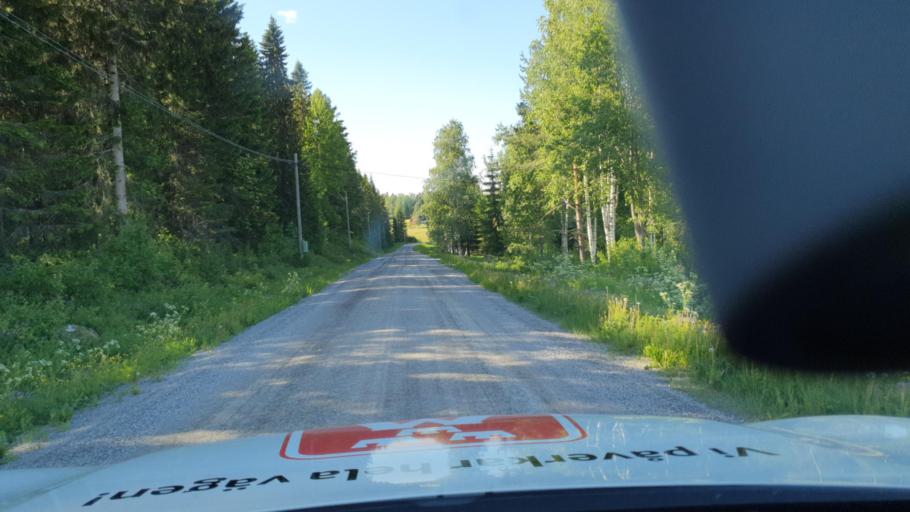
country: SE
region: Vaesterbotten
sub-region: Vannas Kommun
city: Vaennaes
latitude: 63.8117
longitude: 19.6341
